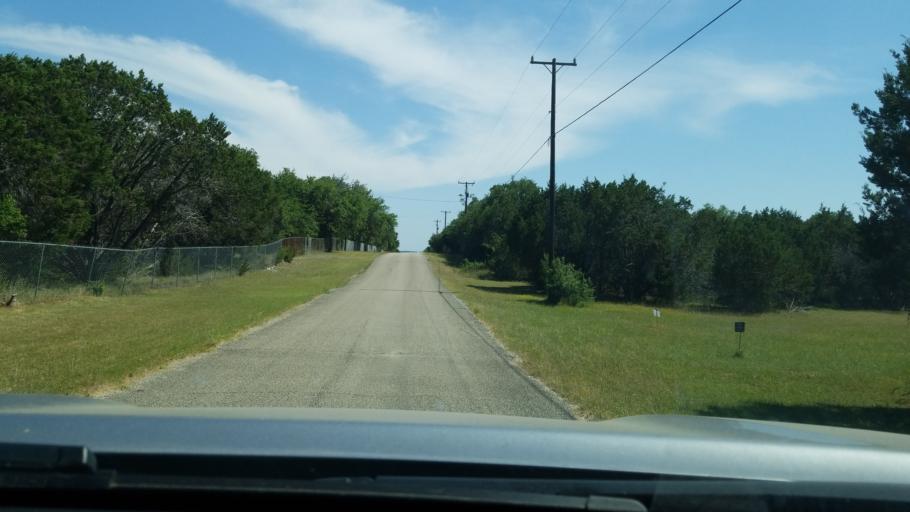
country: US
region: Texas
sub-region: Comal County
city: Bulverde
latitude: 29.7624
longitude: -98.5179
